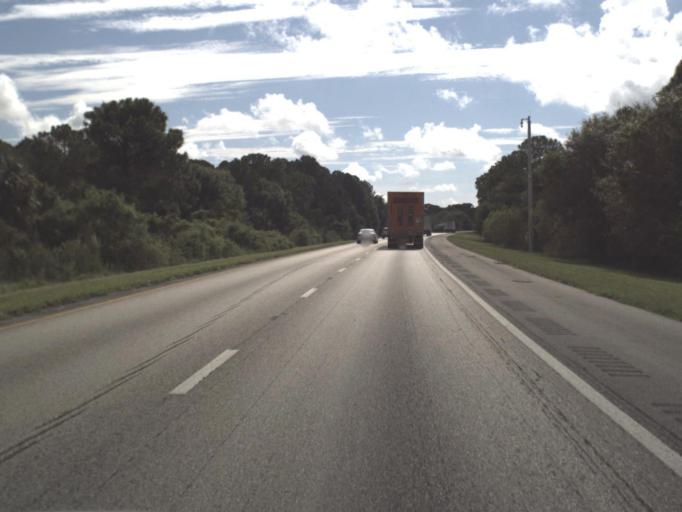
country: US
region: Florida
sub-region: Sarasota County
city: North Port
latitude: 27.0981
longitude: -82.1354
